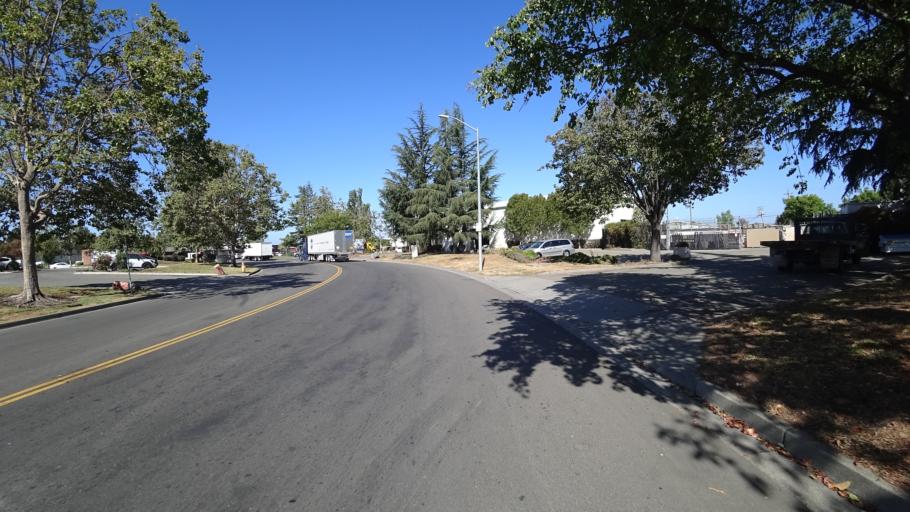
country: US
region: California
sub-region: Alameda County
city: Union City
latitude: 37.6216
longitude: -122.0552
